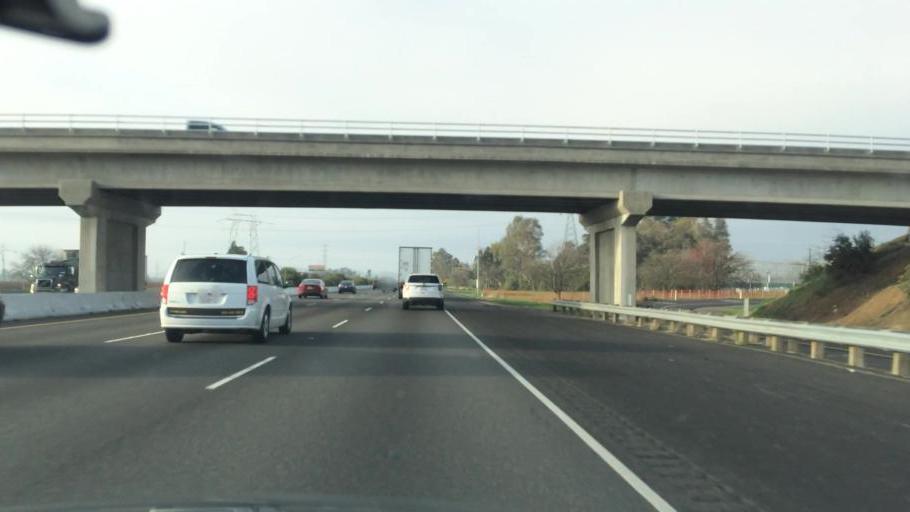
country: US
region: California
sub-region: Solano County
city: Hartley
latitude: 38.4040
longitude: -121.9137
